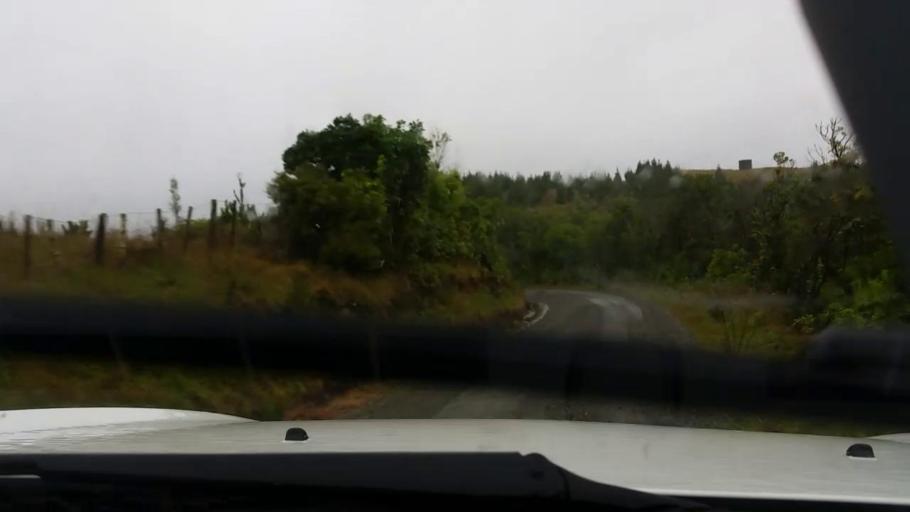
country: NZ
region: Wellington
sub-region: Masterton District
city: Masterton
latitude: -41.2051
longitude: 175.8136
